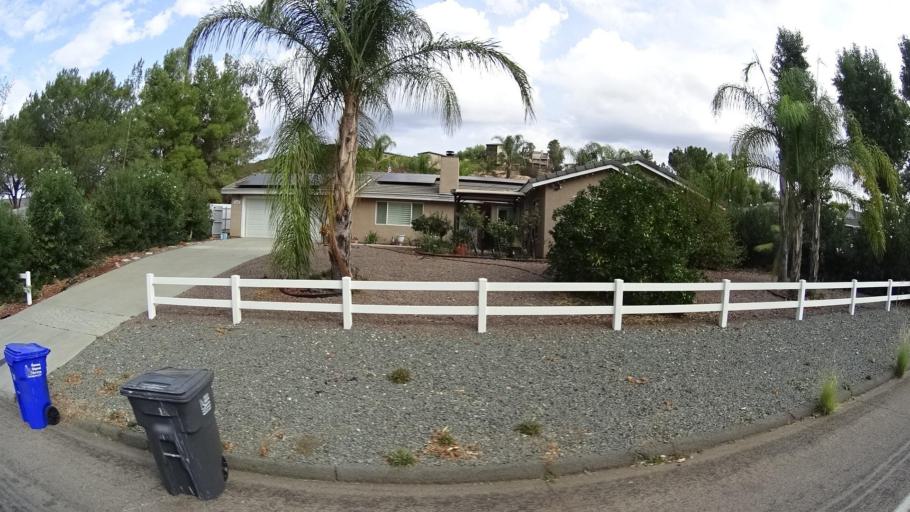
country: US
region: California
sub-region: San Diego County
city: San Diego Country Estates
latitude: 33.0095
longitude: -116.8024
